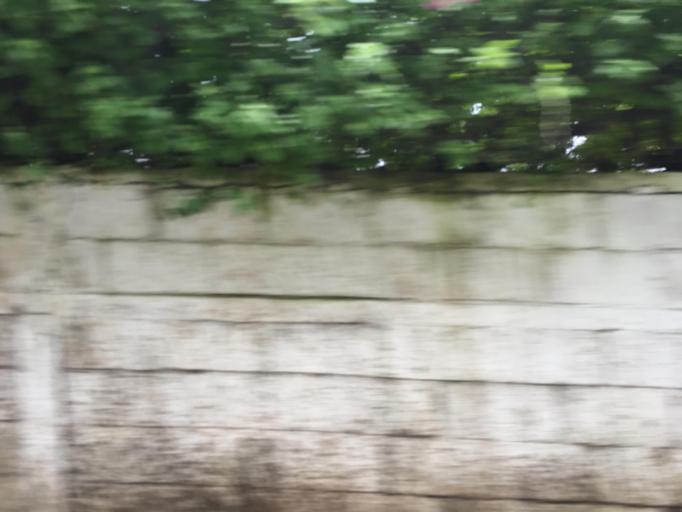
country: GT
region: Guatemala
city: Villa Canales
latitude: 14.4424
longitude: -90.5612
